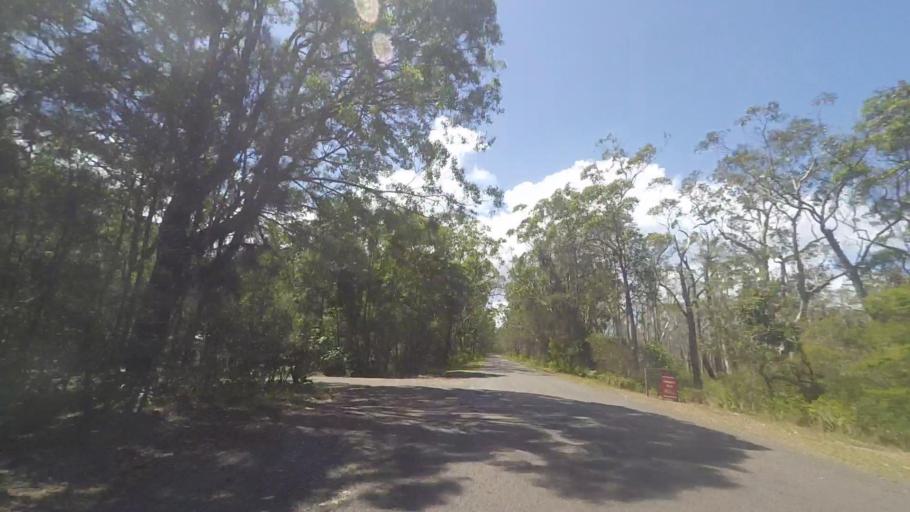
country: AU
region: New South Wales
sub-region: Great Lakes
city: Bulahdelah
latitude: -32.5251
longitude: 152.3229
